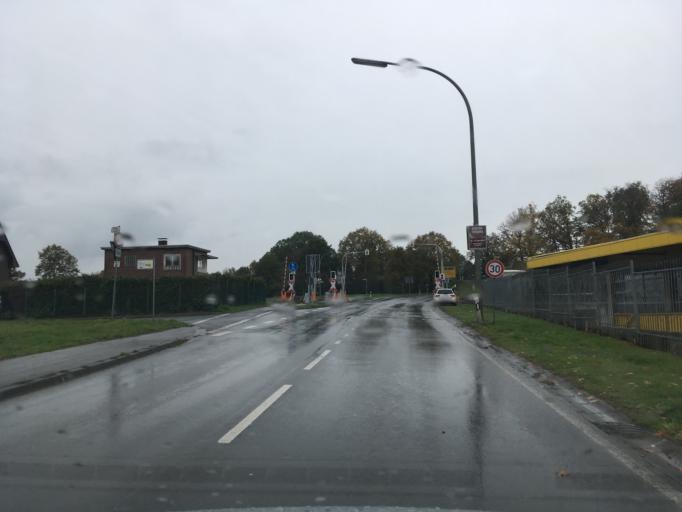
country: DE
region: North Rhine-Westphalia
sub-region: Regierungsbezirk Munster
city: Klein Reken
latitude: 51.8057
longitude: 7.0550
